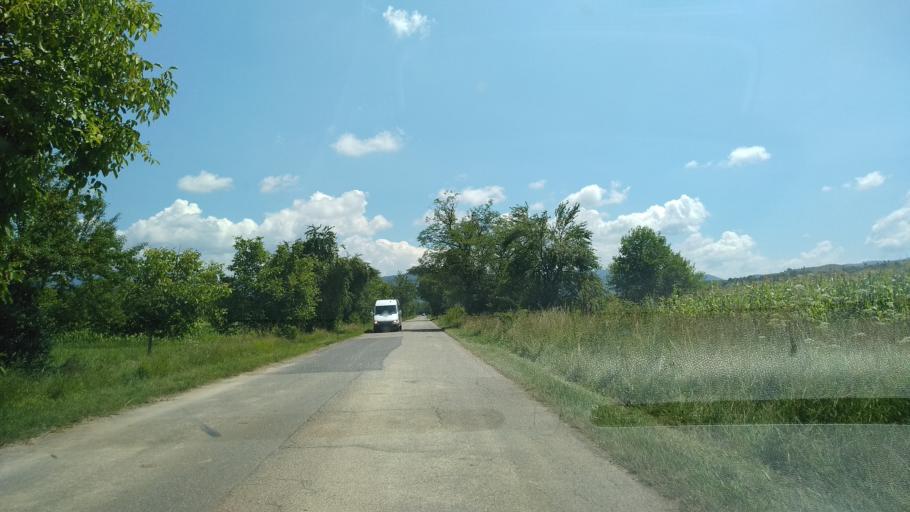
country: RO
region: Hunedoara
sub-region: Comuna Bosorod
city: Bosorod
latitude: 45.7090
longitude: 23.0493
